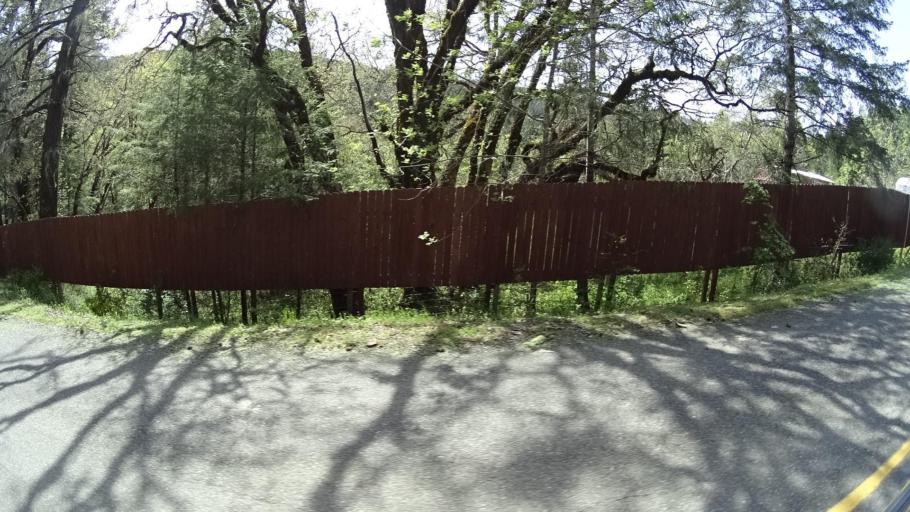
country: US
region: California
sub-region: Humboldt County
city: Redway
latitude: 40.3535
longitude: -123.7188
